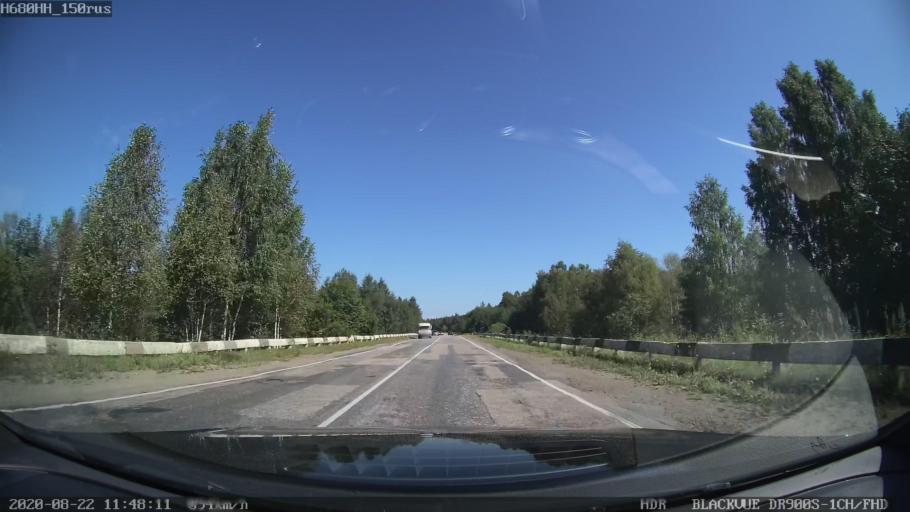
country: RU
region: Tverskaya
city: Sakharovo
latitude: 57.0603
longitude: 36.0993
